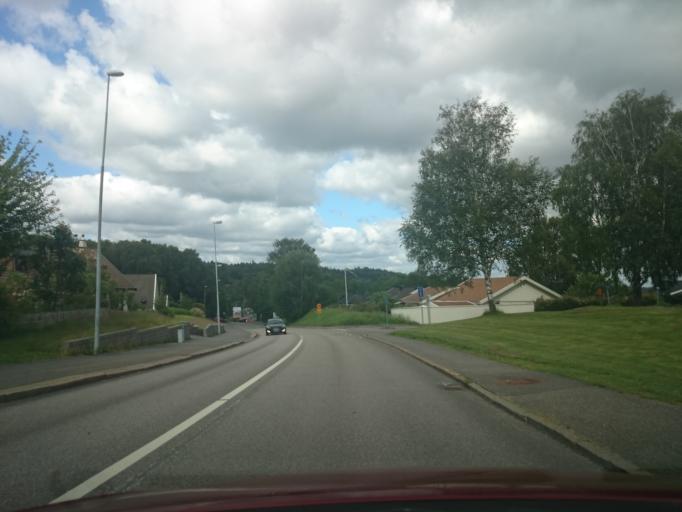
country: SE
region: Vaestra Goetaland
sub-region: Molndal
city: Moelndal
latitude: 57.6613
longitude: 12.0377
